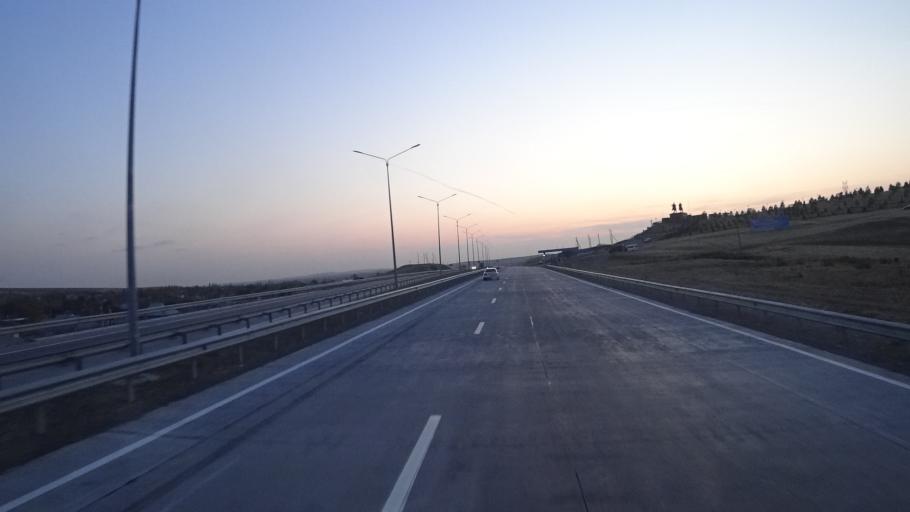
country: KZ
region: Ongtustik Qazaqstan
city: Qazyqurt
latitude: 41.8757
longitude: 69.4302
